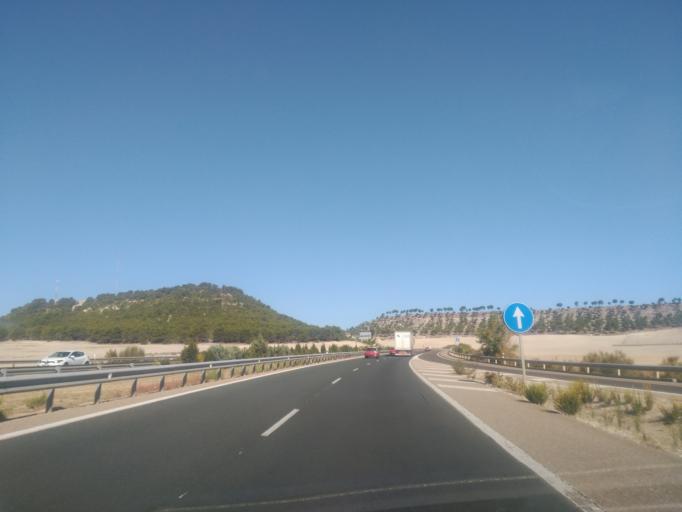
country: ES
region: Castille and Leon
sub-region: Provincia de Valladolid
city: Cisterniga
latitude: 41.6029
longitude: -4.6625
